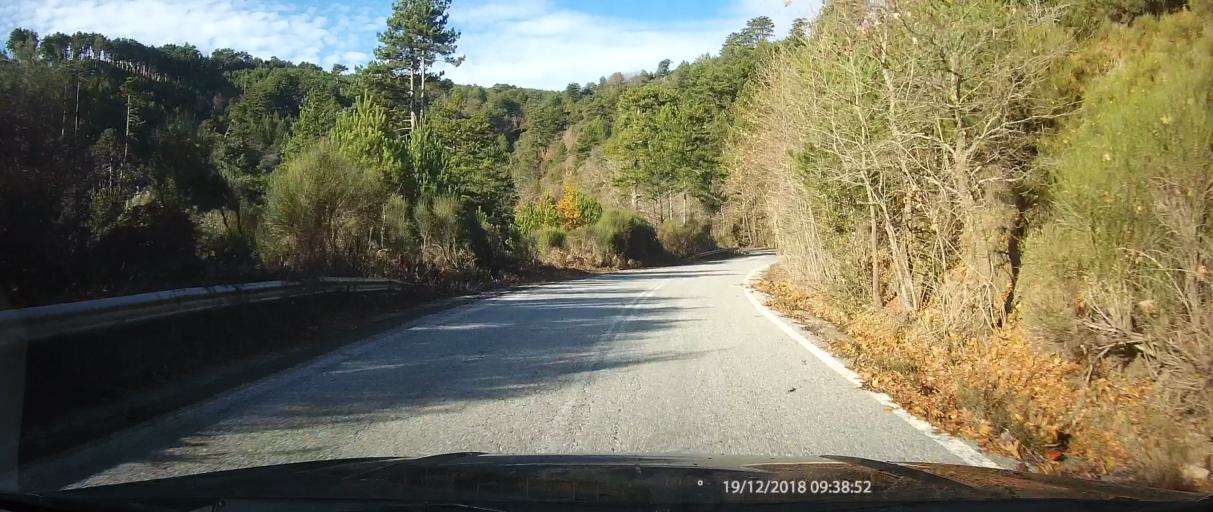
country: GR
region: Peloponnese
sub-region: Nomos Lakonias
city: Magoula
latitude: 37.0807
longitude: 22.2722
